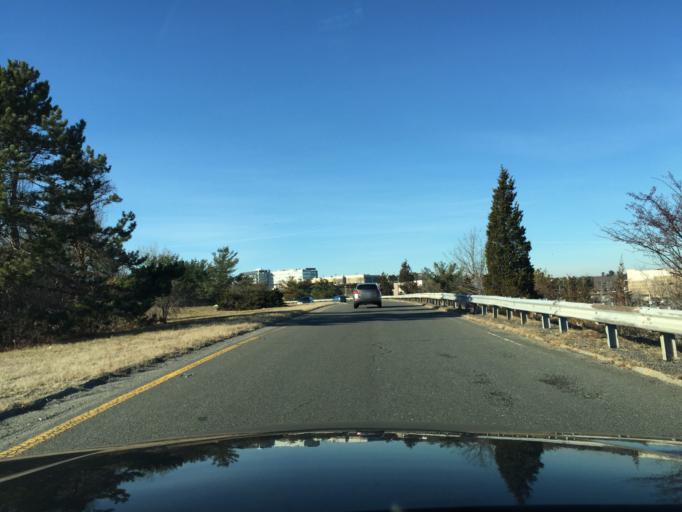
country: US
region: Massachusetts
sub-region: Middlesex County
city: Burlington
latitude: 42.4791
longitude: -71.2132
